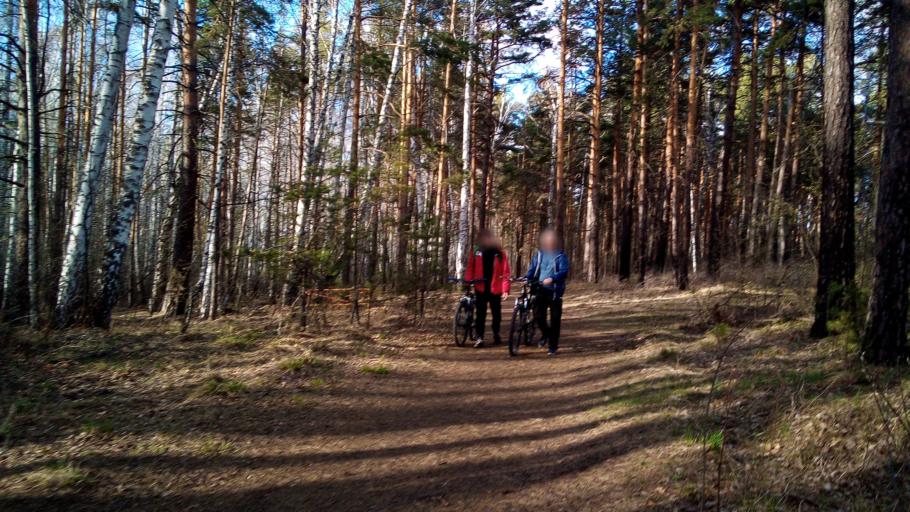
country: RU
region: Chelyabinsk
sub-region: Gorod Chelyabinsk
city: Chelyabinsk
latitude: 55.1632
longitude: 61.3205
